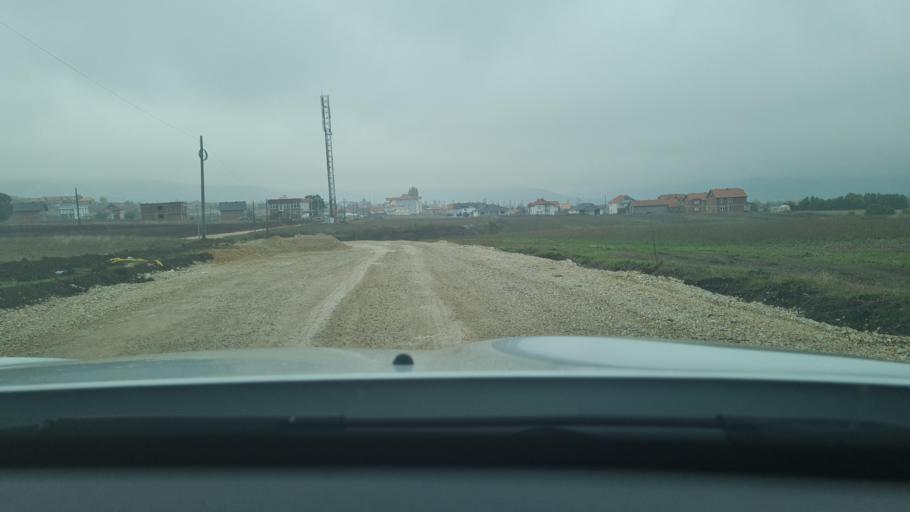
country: MK
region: Opstina Lipkovo
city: Matejche
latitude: 42.1152
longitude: 21.6092
